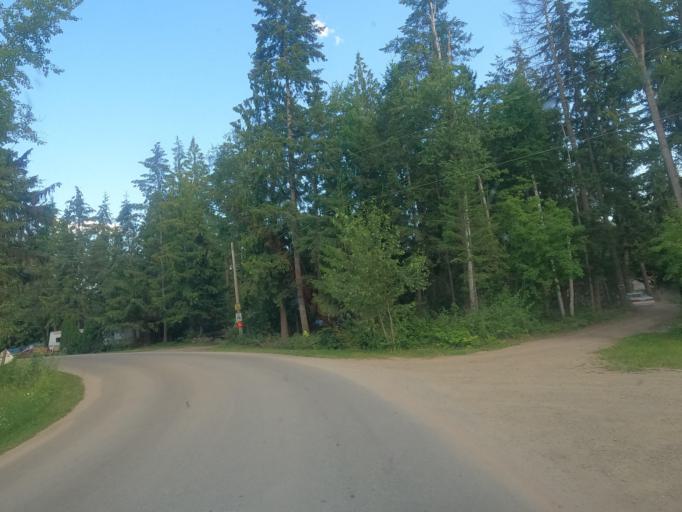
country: CA
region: British Columbia
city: Salmon Arm
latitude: 50.7303
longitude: -119.3128
